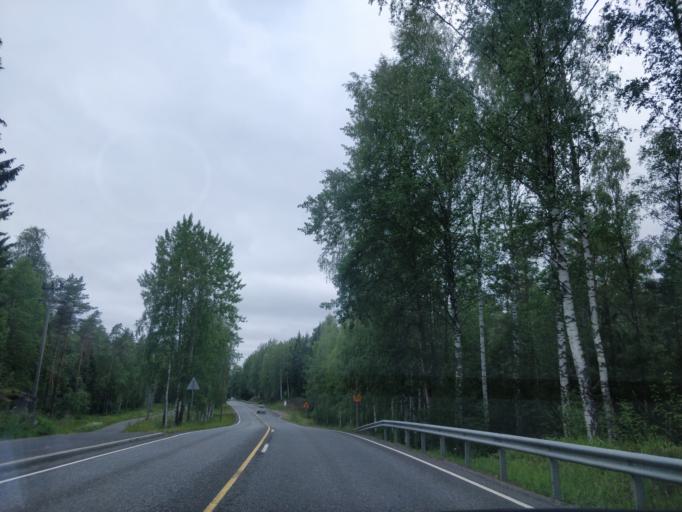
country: FI
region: Uusimaa
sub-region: Helsinki
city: Kauniainen
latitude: 60.3108
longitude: 24.7290
